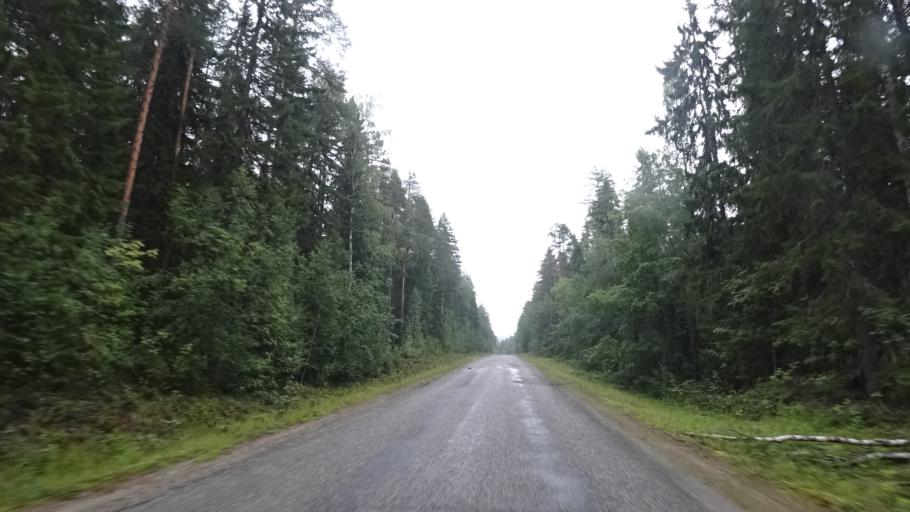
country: FI
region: North Karelia
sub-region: Joensuu
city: Ilomantsi
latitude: 63.2276
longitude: 30.8499
